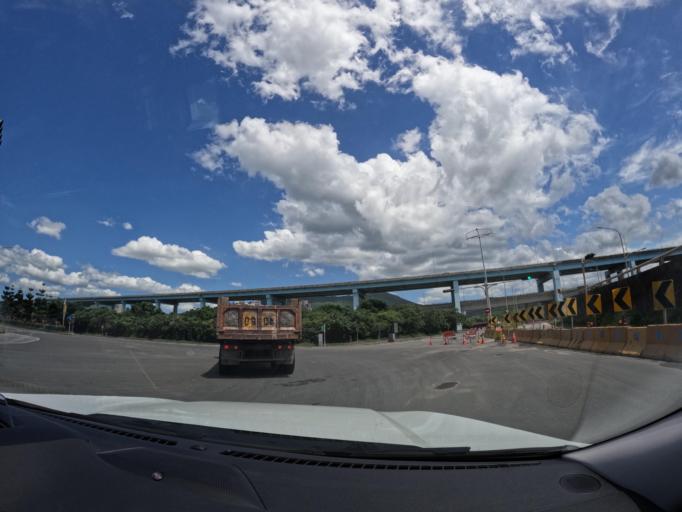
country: TW
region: Taipei
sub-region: Taipei
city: Banqiao
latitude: 25.1493
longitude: 121.3894
